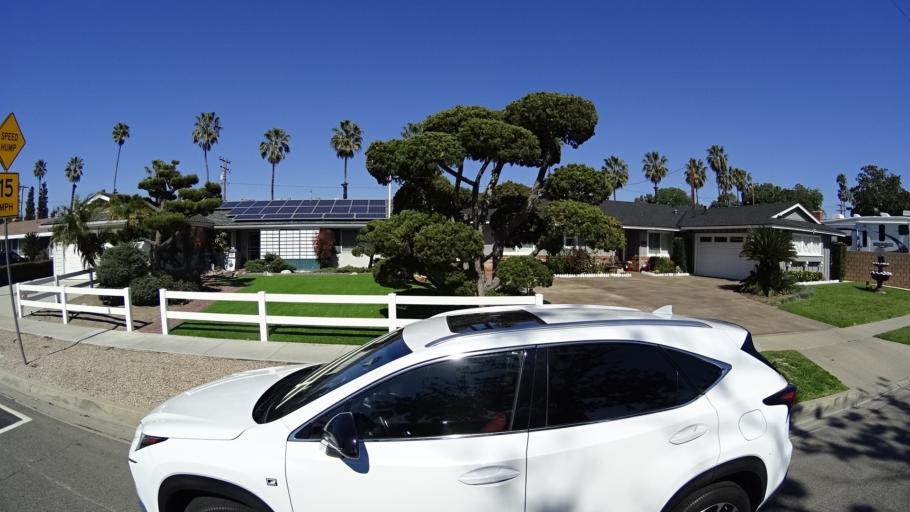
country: US
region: California
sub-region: Orange County
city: Anaheim
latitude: 33.8138
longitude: -117.9382
